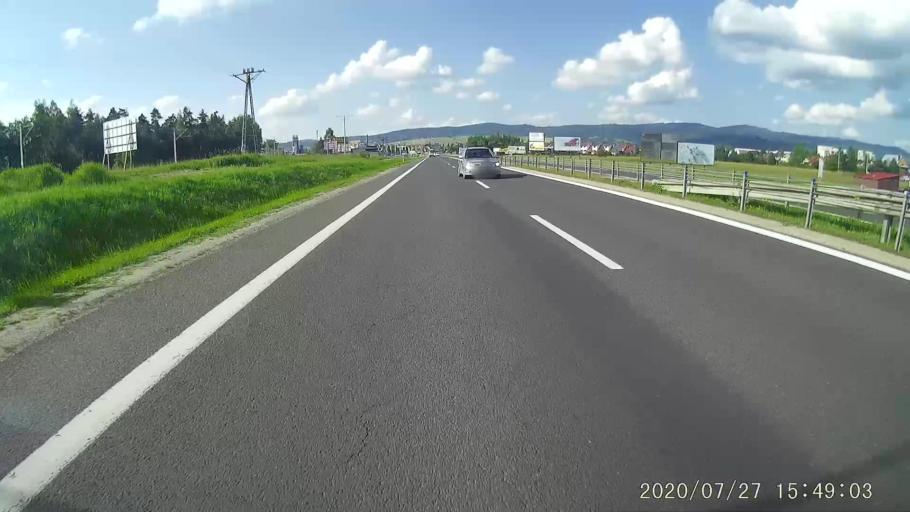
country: PL
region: Lesser Poland Voivodeship
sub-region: Powiat nowotarski
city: Nowy Targ
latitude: 49.4666
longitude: 20.0205
